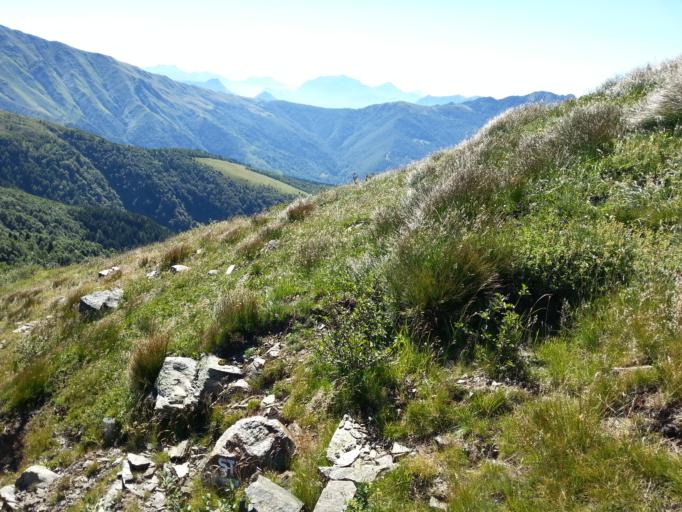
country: CH
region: Ticino
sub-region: Bellinzona District
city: Camorino
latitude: 46.1088
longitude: 9.0161
